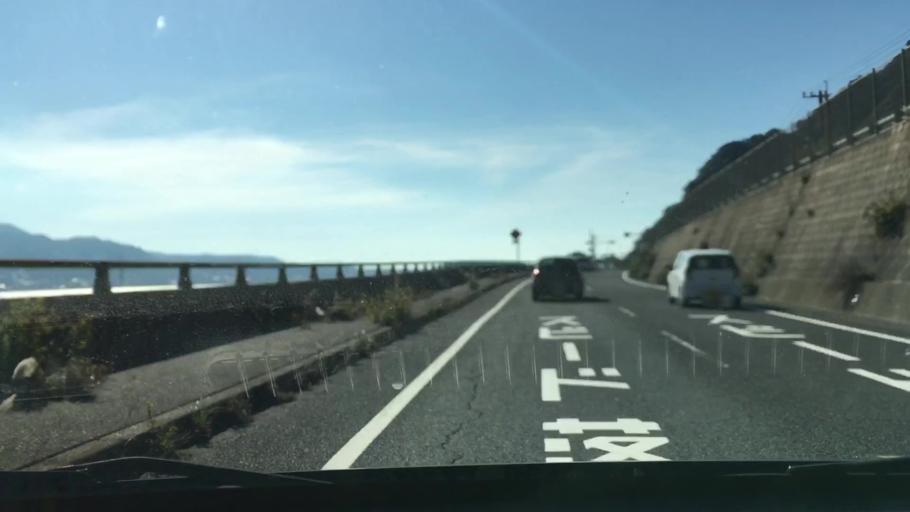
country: JP
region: Kagoshima
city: Kagoshima-shi
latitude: 31.6383
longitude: 130.6027
